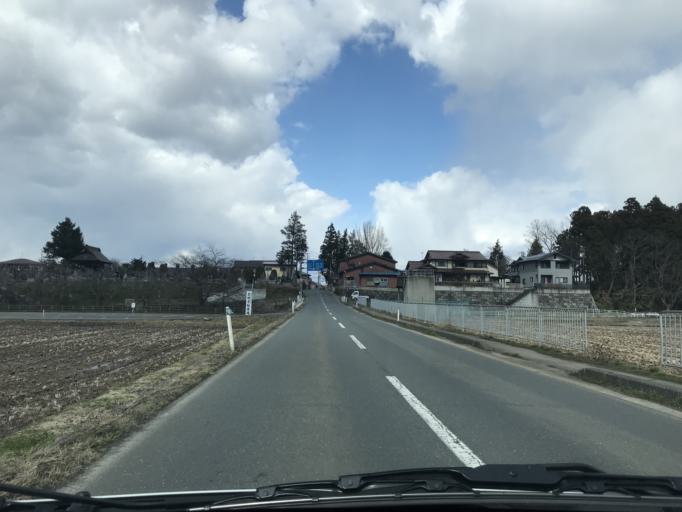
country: JP
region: Iwate
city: Kitakami
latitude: 39.2942
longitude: 141.0695
